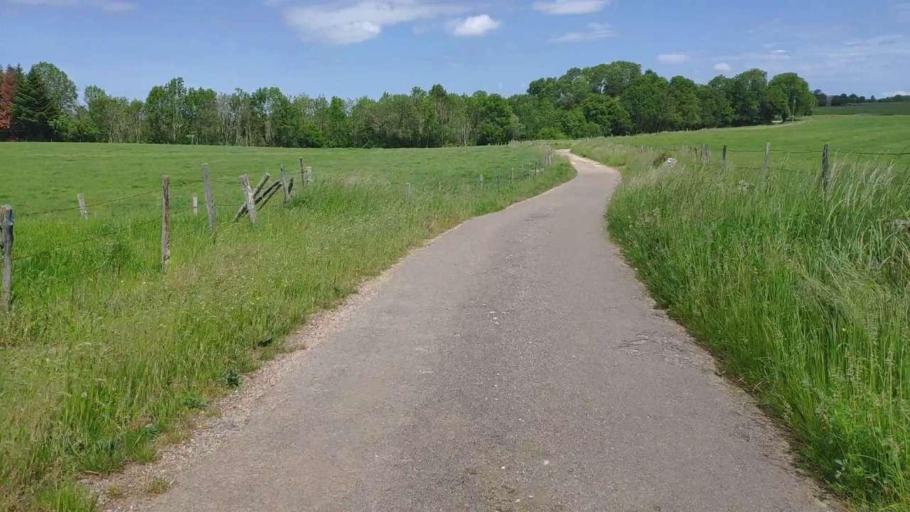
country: FR
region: Franche-Comte
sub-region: Departement du Jura
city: Perrigny
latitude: 46.7513
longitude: 5.6350
